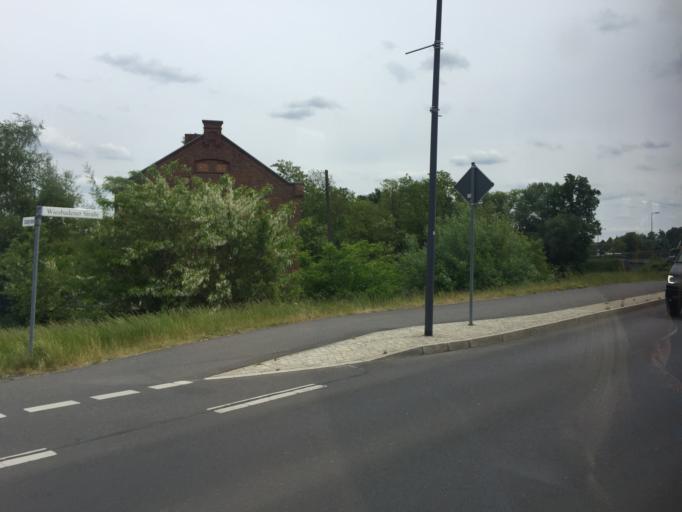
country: DE
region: Saxony
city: Goerlitz
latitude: 51.1528
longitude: 14.9505
